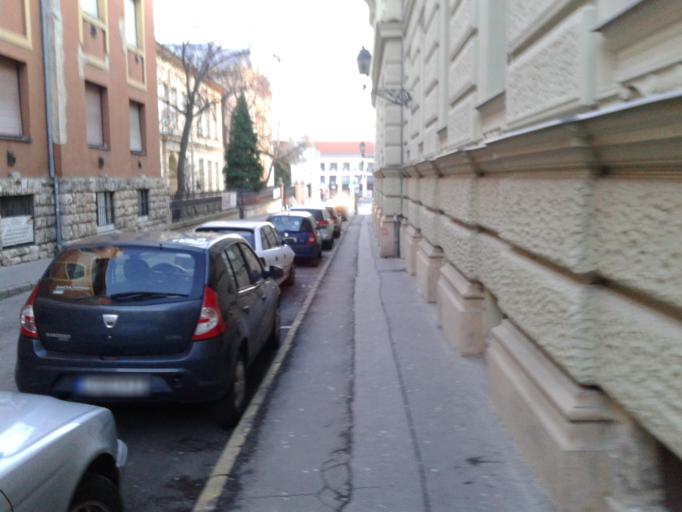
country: HU
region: Baranya
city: Pecs
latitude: 46.0748
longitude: 18.2305
